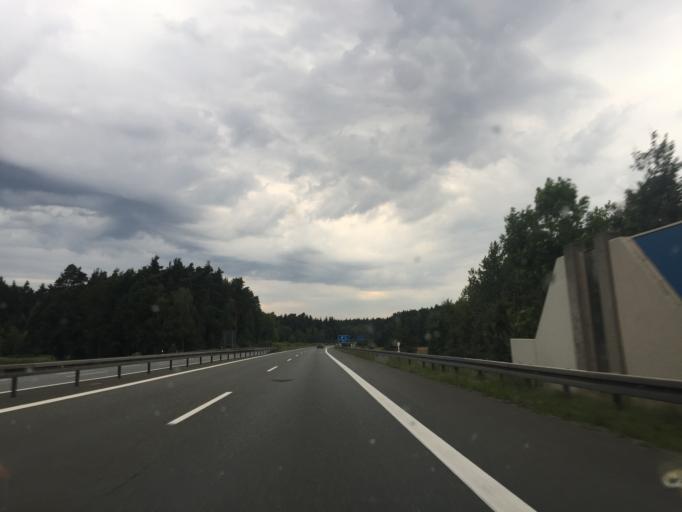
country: DE
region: Bavaria
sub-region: Upper Palatinate
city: Weiden
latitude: 49.6747
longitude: 12.1305
